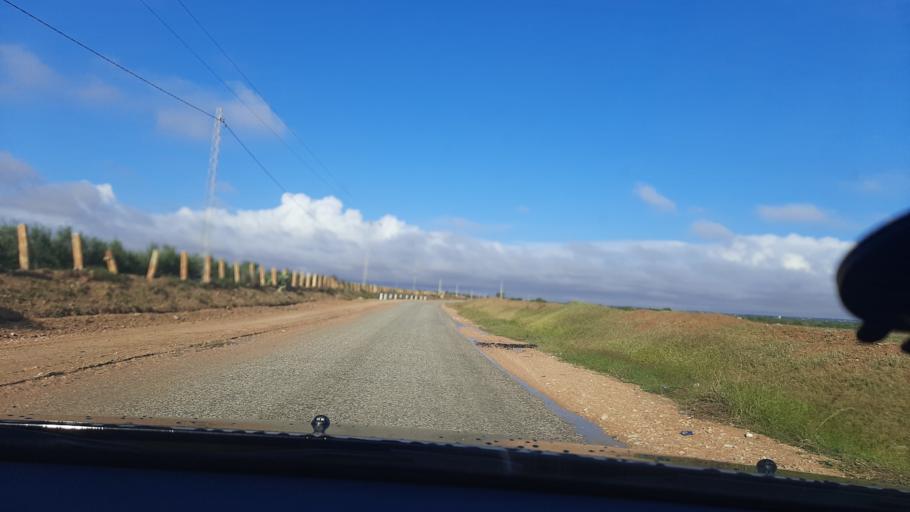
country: TN
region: Safaqis
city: Sfax
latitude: 34.8882
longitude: 10.6235
